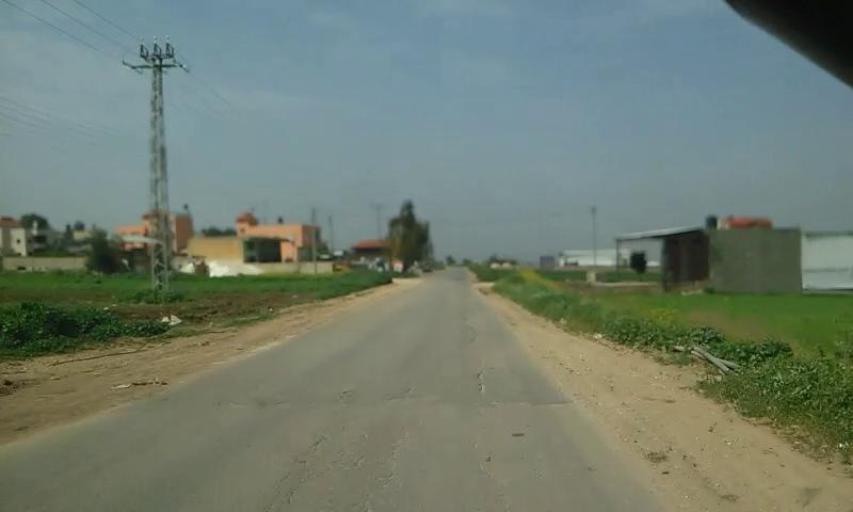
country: PS
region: West Bank
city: Kafr Dan
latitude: 32.4928
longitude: 35.2573
